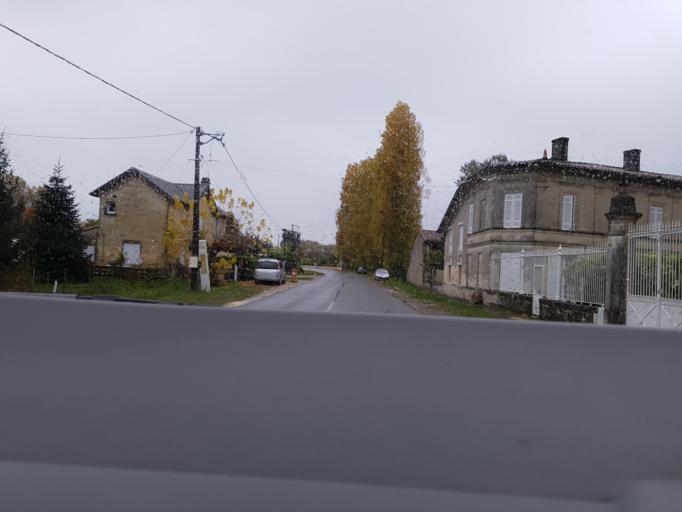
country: FR
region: Aquitaine
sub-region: Departement de la Gironde
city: Aubie-et-Espessas
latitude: 45.0205
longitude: -0.4236
